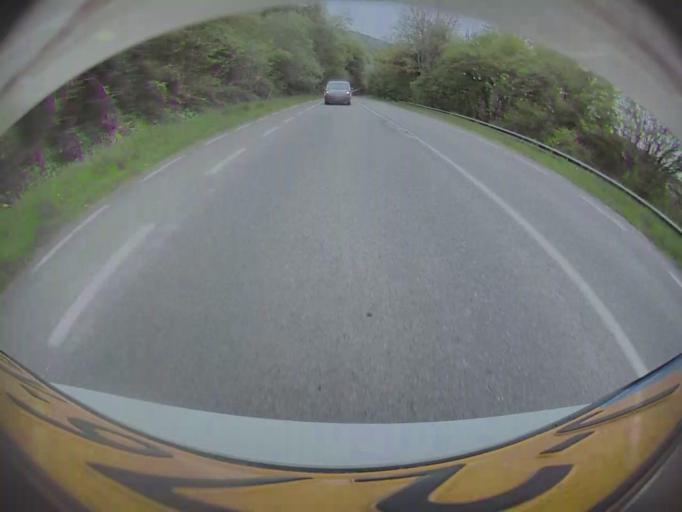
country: BE
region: Wallonia
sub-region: Province de Liege
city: Hamoir
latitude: 50.4122
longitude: 5.5079
